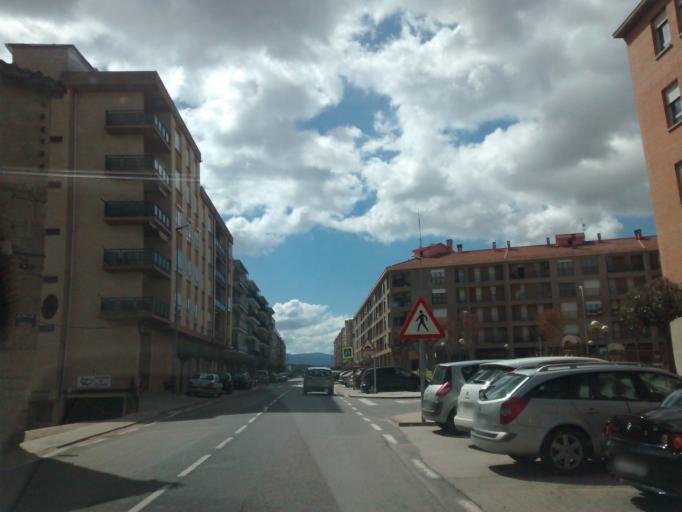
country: ES
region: La Rioja
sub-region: Provincia de La Rioja
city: Fuenmayor
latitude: 42.4662
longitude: -2.5613
